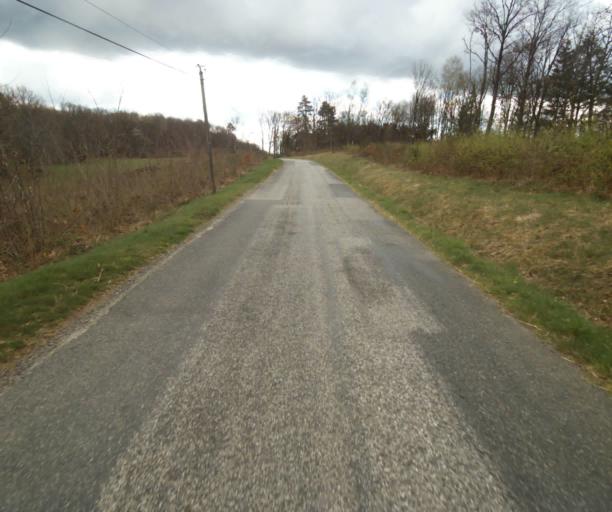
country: FR
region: Limousin
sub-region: Departement de la Correze
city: Correze
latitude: 45.2684
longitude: 1.8959
